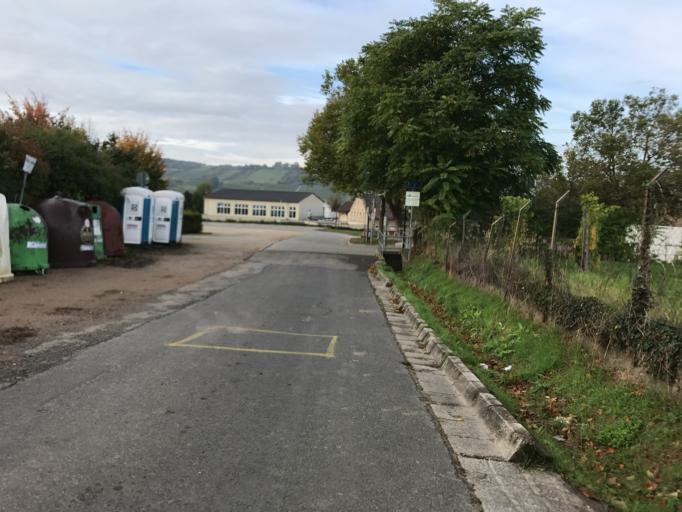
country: DE
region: Rheinland-Pfalz
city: Ingelheim am Rhein
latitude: 49.9635
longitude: 8.0653
